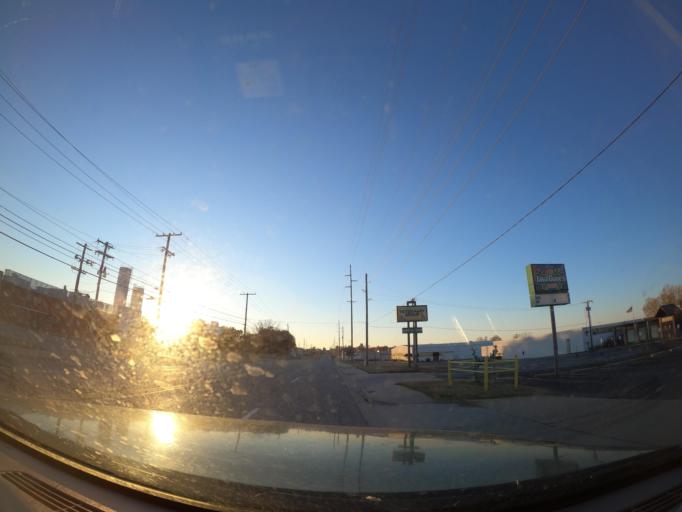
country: US
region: Oklahoma
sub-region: Tulsa County
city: Tulsa
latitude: 36.1407
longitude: -95.9065
